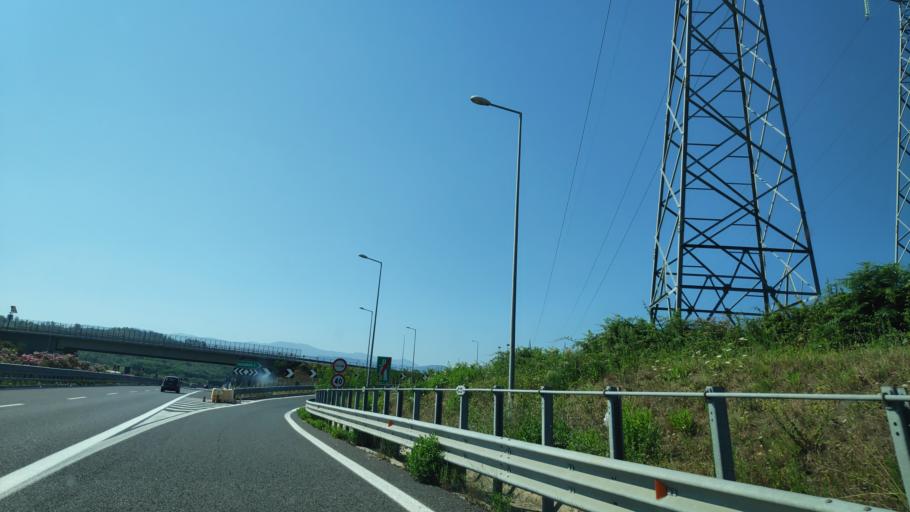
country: IT
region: Calabria
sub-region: Provincia di Reggio Calabria
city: Ceramida-Pellegrina
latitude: 38.3137
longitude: 15.8424
